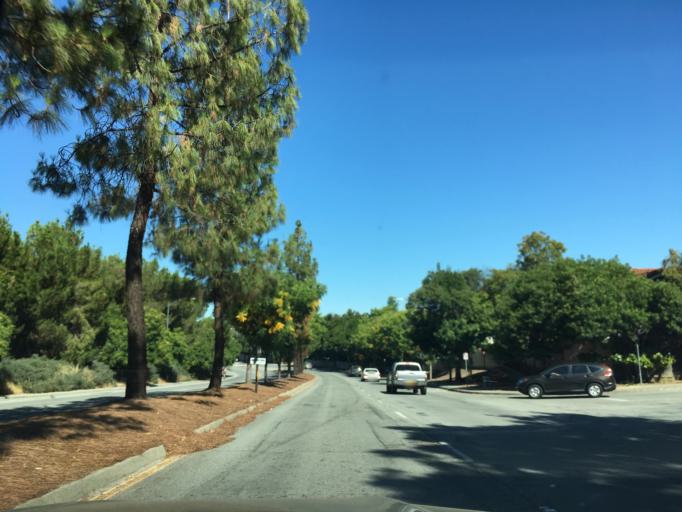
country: US
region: California
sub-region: Santa Clara County
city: Seven Trees
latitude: 37.2420
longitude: -121.8648
